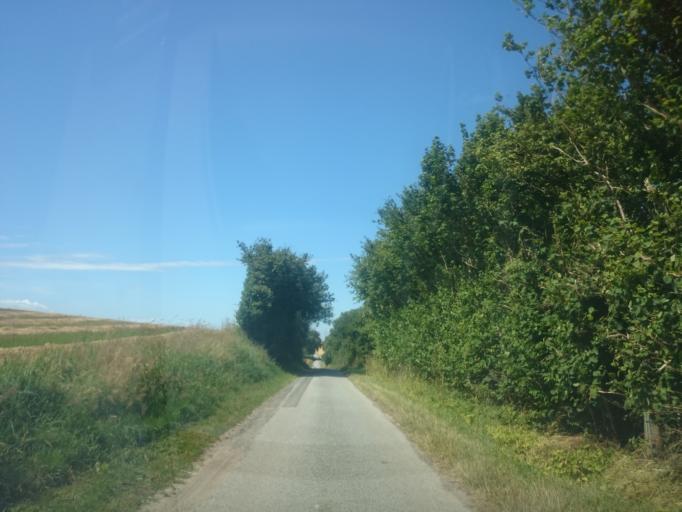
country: DK
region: South Denmark
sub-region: Langeland Kommune
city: Rudkobing
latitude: 54.9639
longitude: 10.8440
